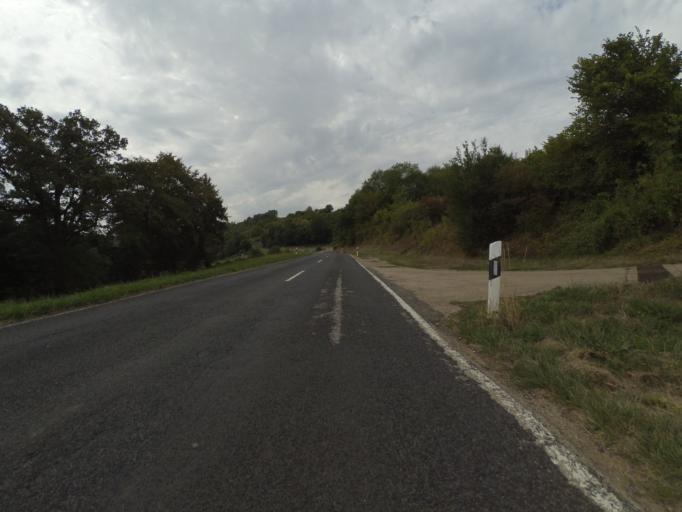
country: DE
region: Rheinland-Pfalz
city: Onsdorf
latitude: 49.6509
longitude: 6.4860
